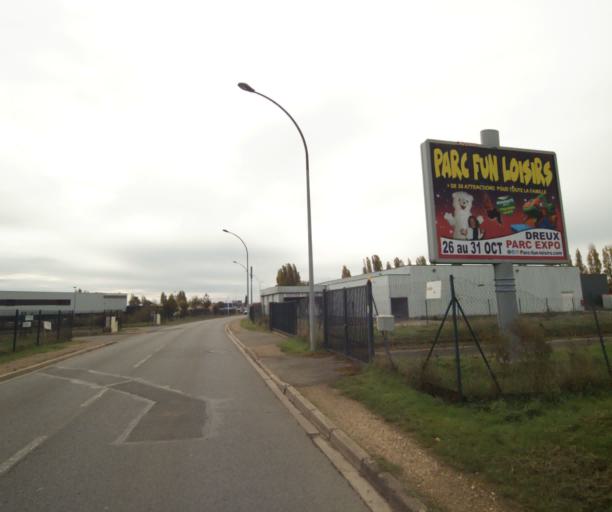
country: FR
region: Centre
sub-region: Departement d'Eure-et-Loir
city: Dreux
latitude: 48.7494
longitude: 1.3625
